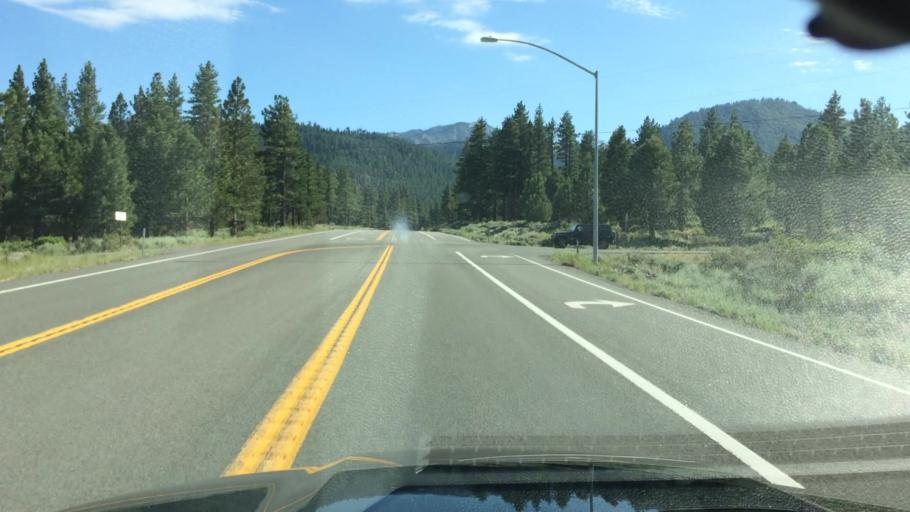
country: US
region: Nevada
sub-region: Washoe County
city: Incline Village
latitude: 39.3641
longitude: -119.8500
